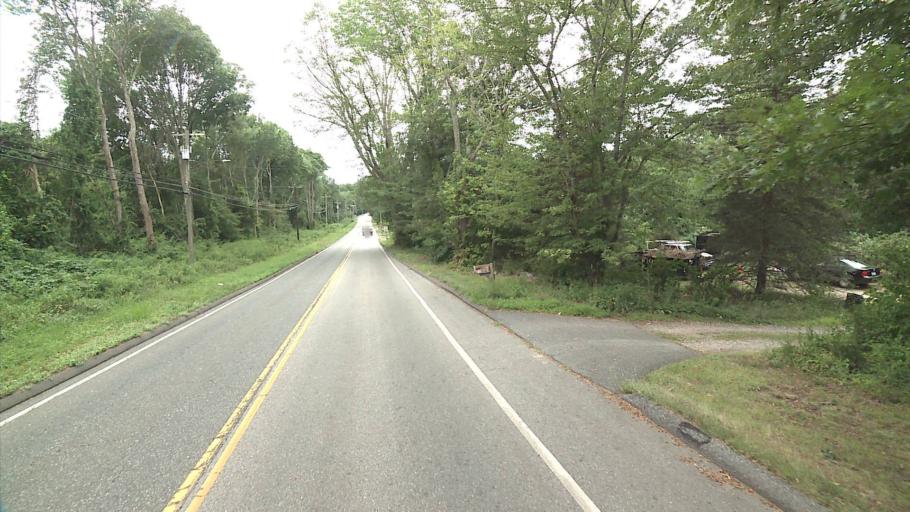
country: US
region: Connecticut
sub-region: New London County
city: Niantic
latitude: 41.3129
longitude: -72.2523
